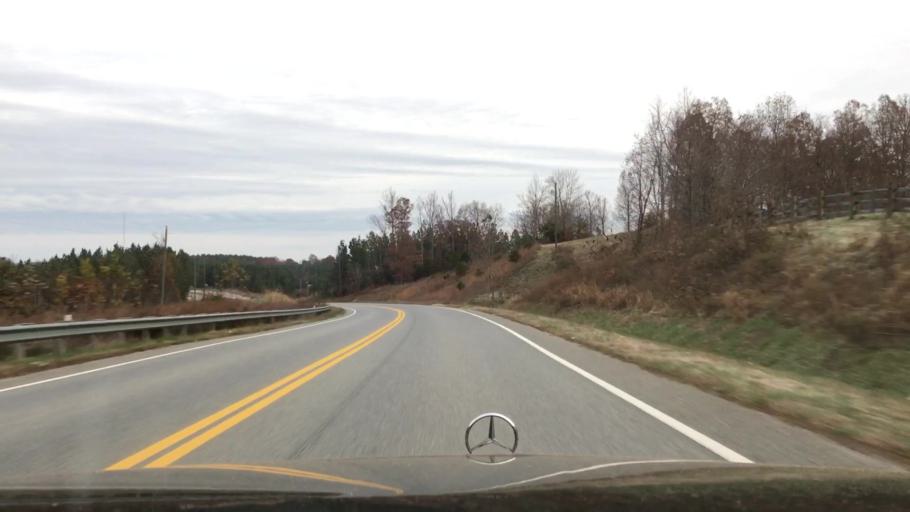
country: US
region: Virginia
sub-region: Campbell County
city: Altavista
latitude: 37.1891
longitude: -79.2937
